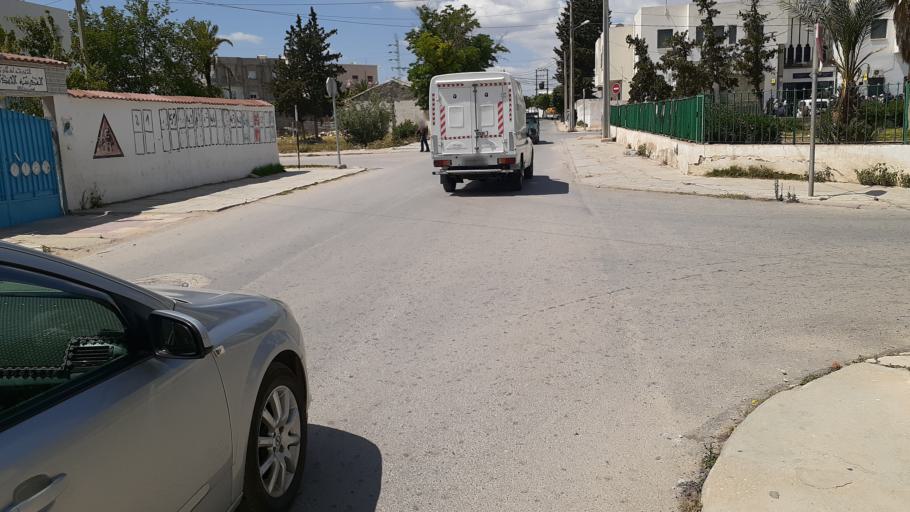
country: TN
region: Silyanah
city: Siliana
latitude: 36.0856
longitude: 9.3725
